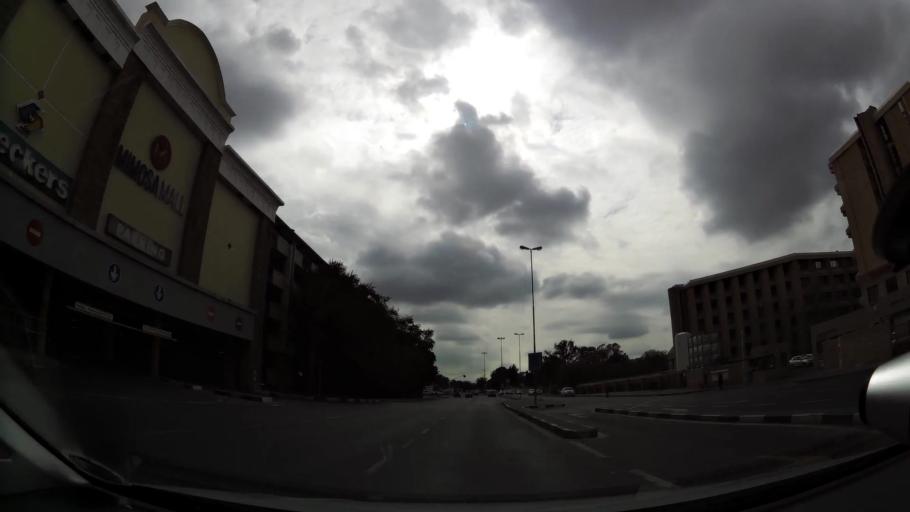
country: ZA
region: Orange Free State
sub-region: Mangaung Metropolitan Municipality
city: Bloemfontein
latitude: -29.1093
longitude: 26.2023
